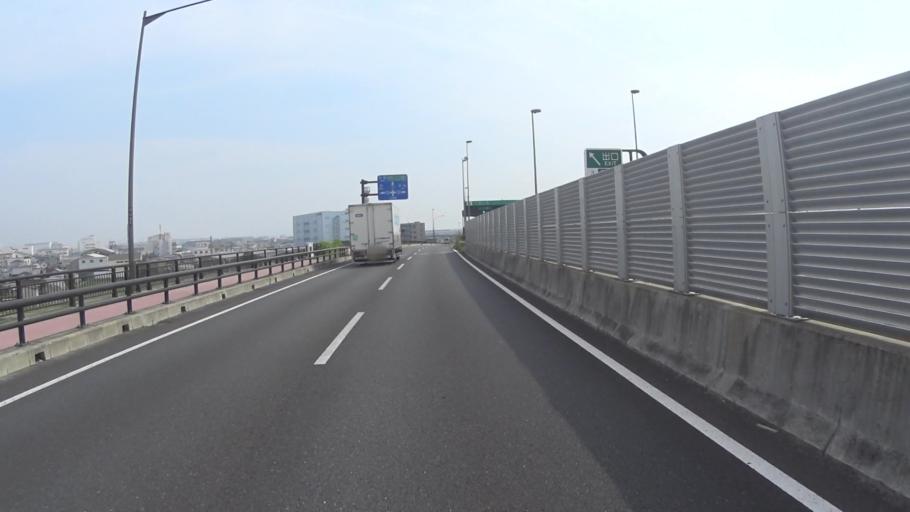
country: JP
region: Kyoto
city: Yawata
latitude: 34.8719
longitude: 135.7434
